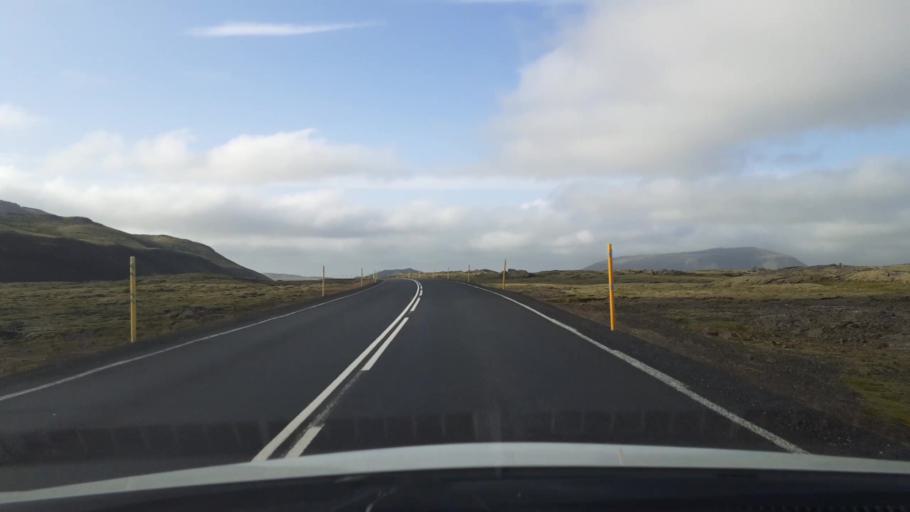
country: IS
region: South
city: THorlakshoefn
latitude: 63.9930
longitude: -21.4638
